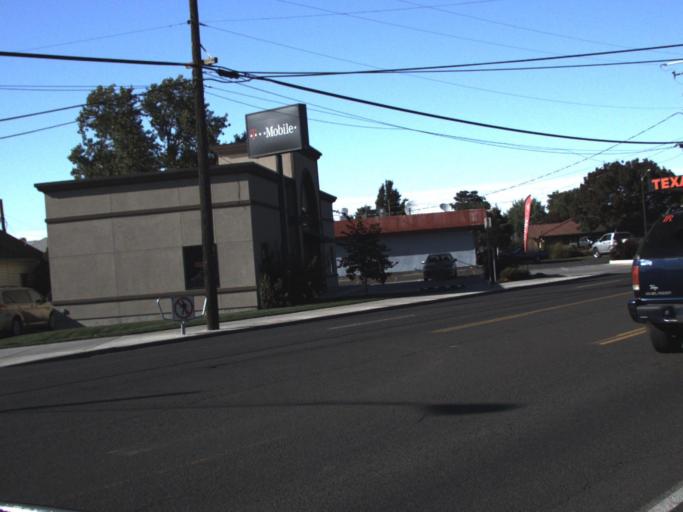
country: US
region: Washington
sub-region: Walla Walla County
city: Walla Walla
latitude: 46.0571
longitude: -118.3461
